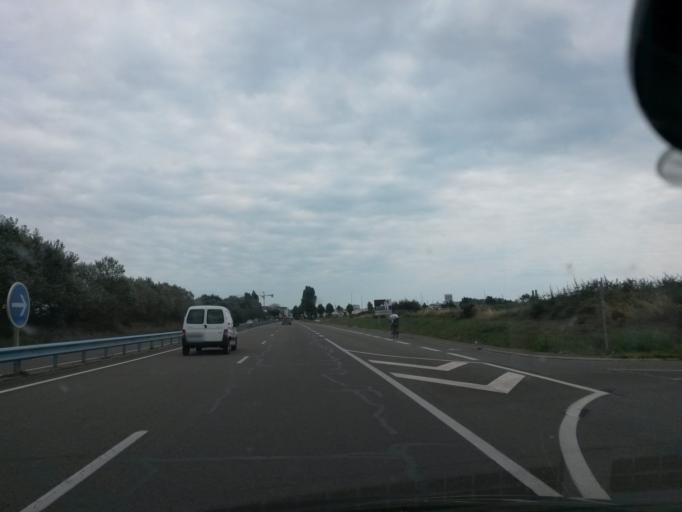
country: FR
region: Pays de la Loire
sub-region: Departement de la Vendee
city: Les Sables-d'Olonne
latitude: 46.5082
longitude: -1.7930
